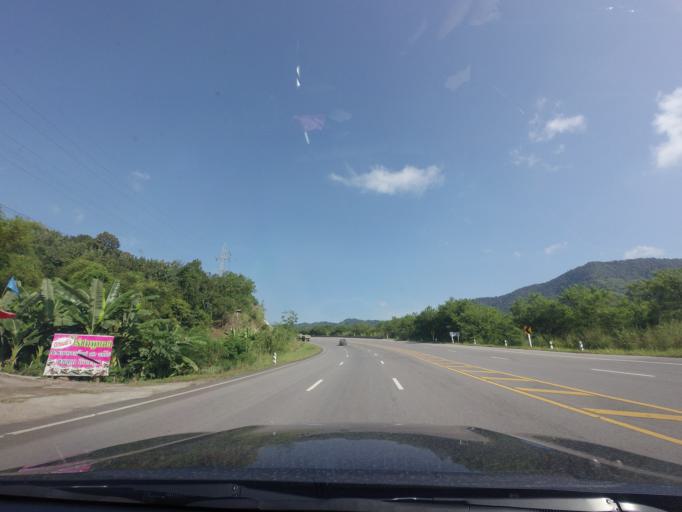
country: TH
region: Phetchabun
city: Lom Sak
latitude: 16.7732
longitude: 101.1216
